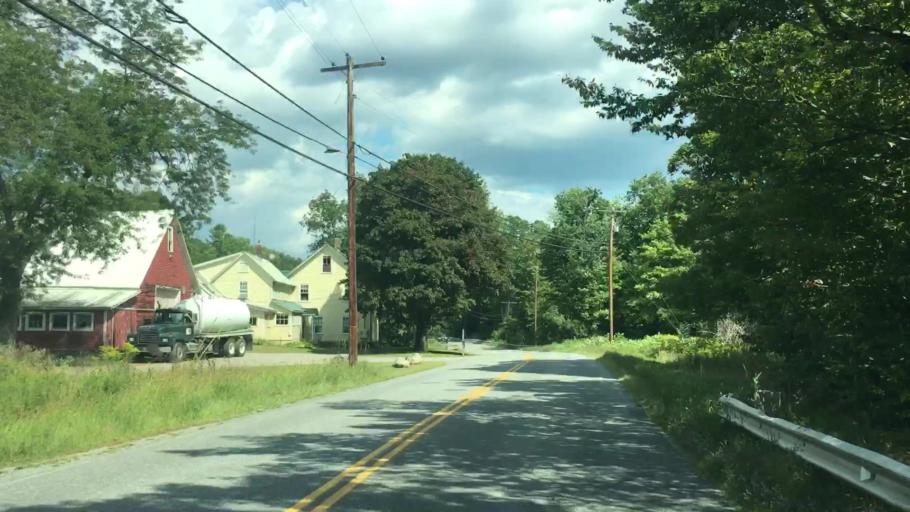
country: US
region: Vermont
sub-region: Windham County
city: Brattleboro
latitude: 42.8135
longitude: -72.5822
